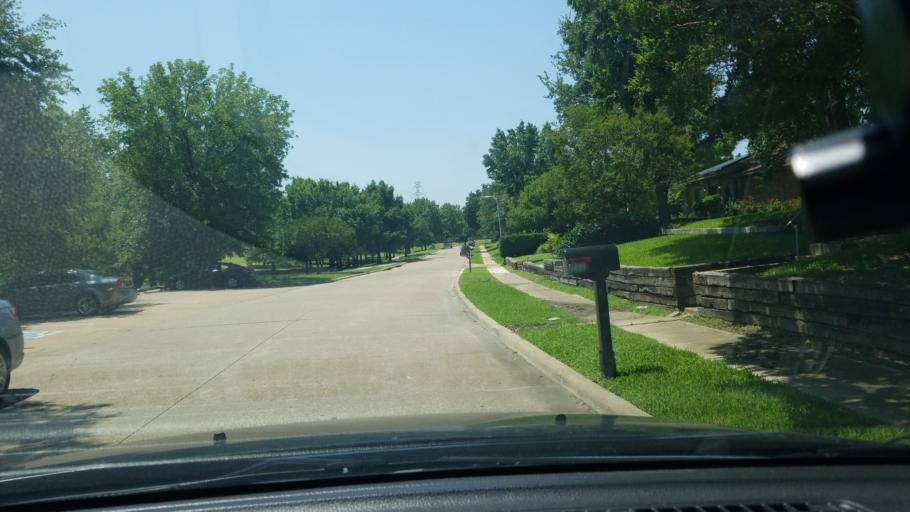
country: US
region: Texas
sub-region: Dallas County
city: Sunnyvale
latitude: 32.8308
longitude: -96.6066
